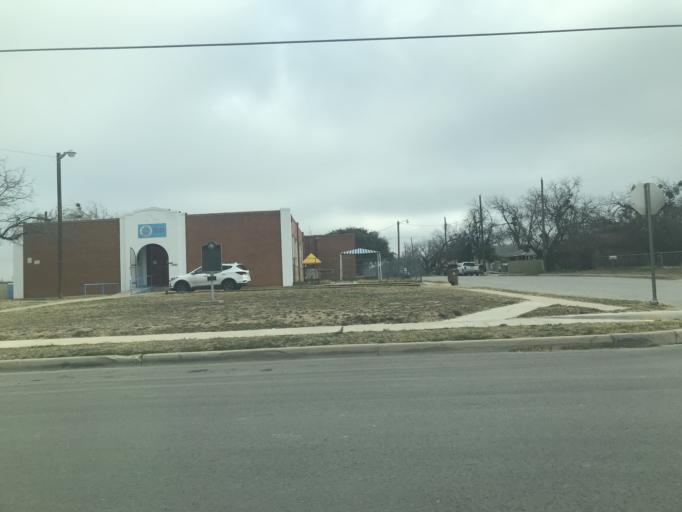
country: US
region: Texas
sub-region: Tom Green County
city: San Angelo
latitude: 31.4709
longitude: -100.4472
